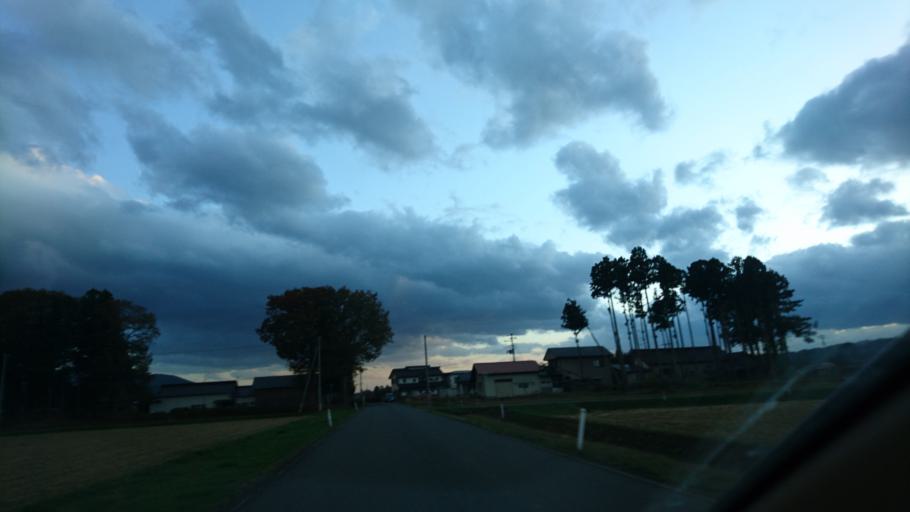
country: JP
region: Iwate
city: Mizusawa
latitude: 39.0734
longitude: 141.1414
